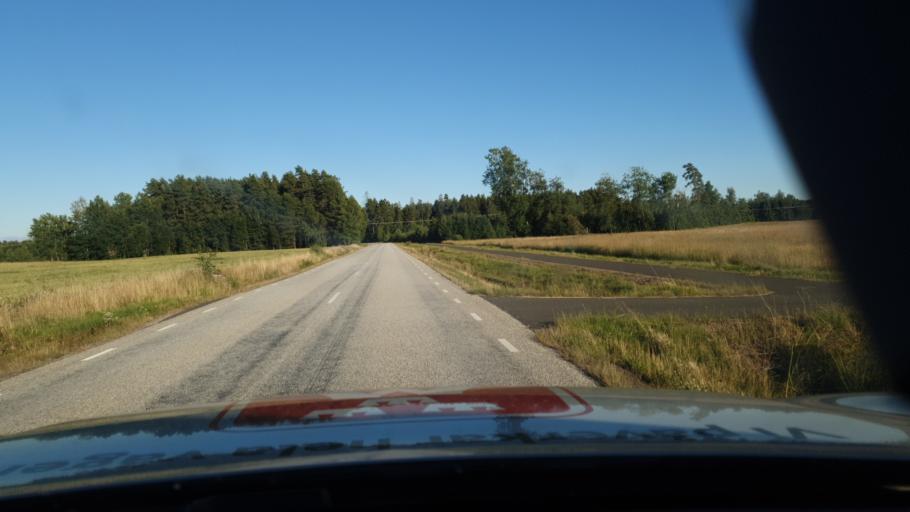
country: SE
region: Vaestra Goetaland
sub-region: Skovde Kommun
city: Stopen
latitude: 58.4755
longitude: 13.9001
